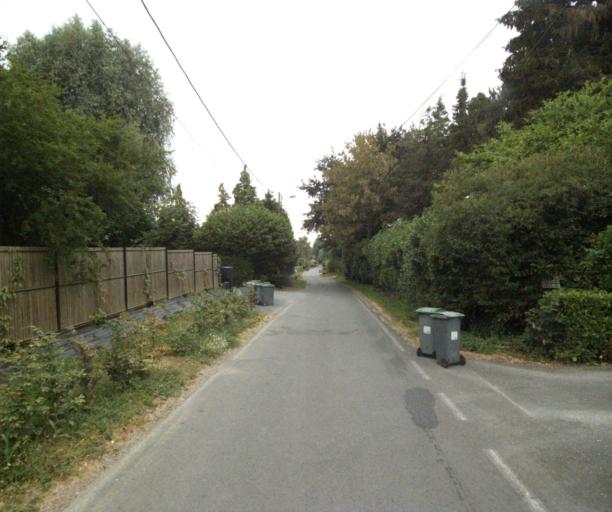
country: FR
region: Nord-Pas-de-Calais
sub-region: Departement du Nord
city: Bondues
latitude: 50.7210
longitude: 3.1015
